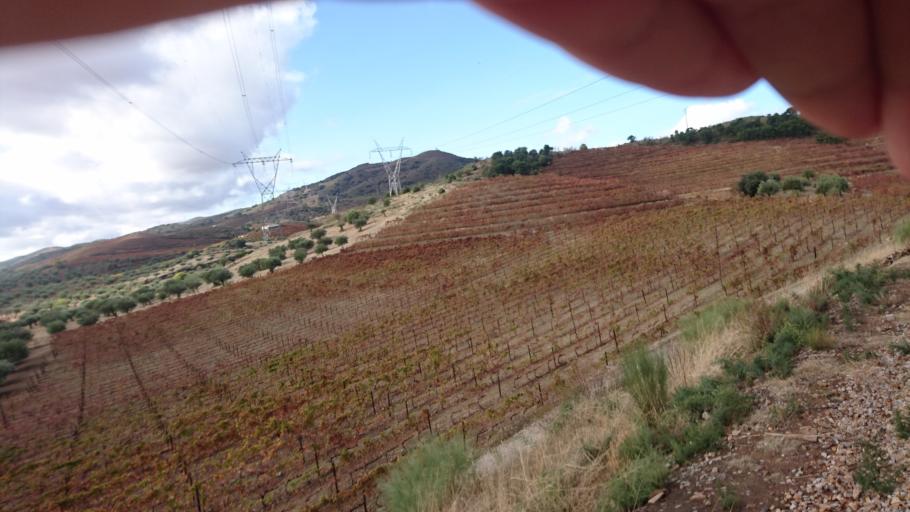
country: PT
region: Guarda
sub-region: Vila Nova de Foz Coa
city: Vila Nova de Foz Coa
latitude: 41.1276
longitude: -7.1345
